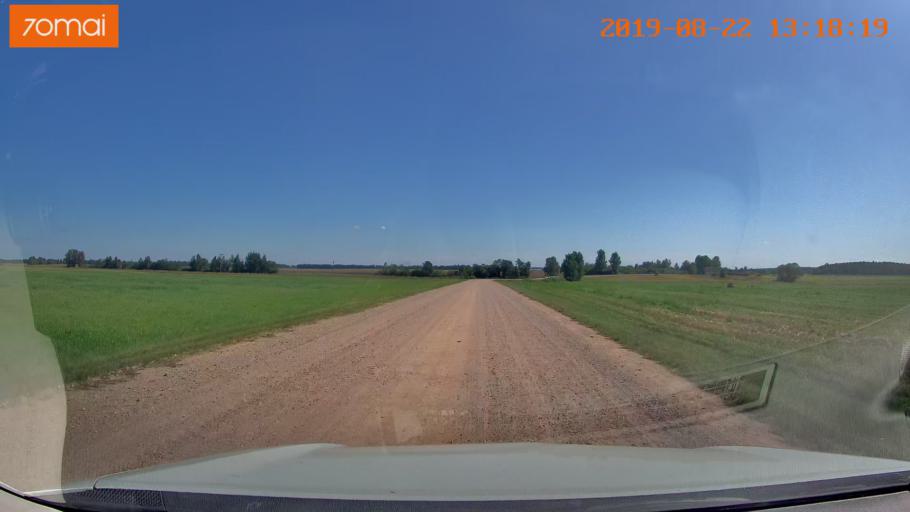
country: BY
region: Minsk
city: Urechcha
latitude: 53.2416
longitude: 27.9374
